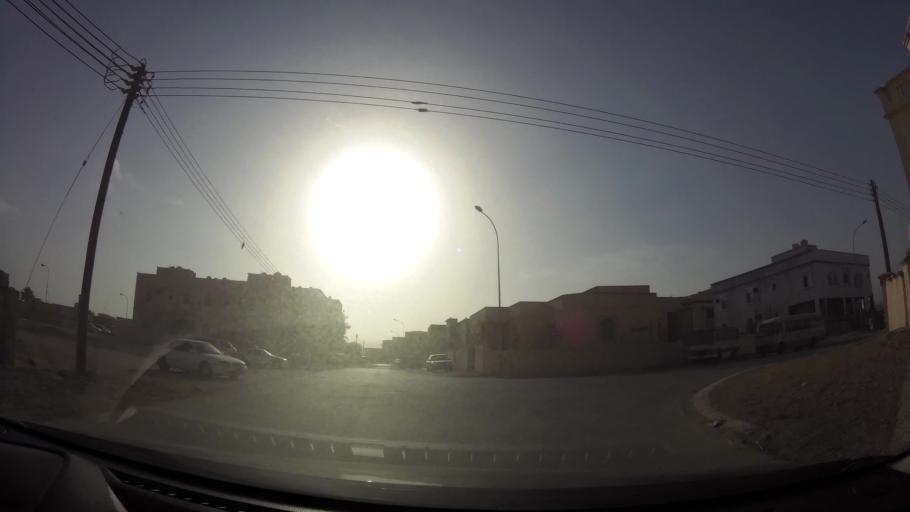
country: OM
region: Zufar
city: Salalah
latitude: 17.0117
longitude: 54.0320
